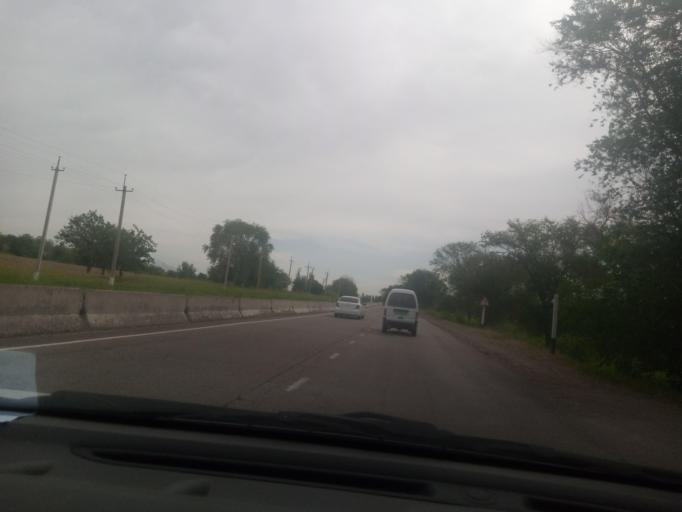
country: UZ
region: Toshkent
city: Ohangaron
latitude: 40.9333
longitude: 69.8839
